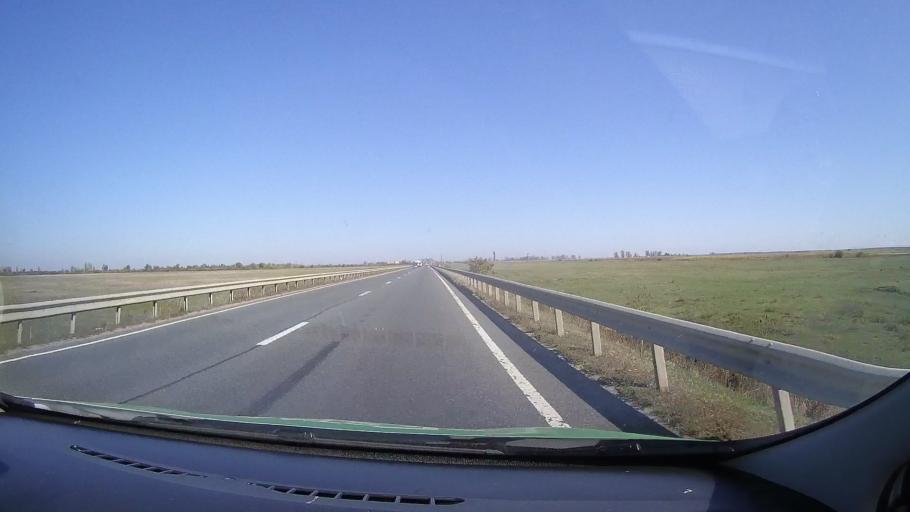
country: RO
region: Satu Mare
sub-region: Comuna Moftinu
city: Moftinu Mic
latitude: 47.6910
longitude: 22.6131
